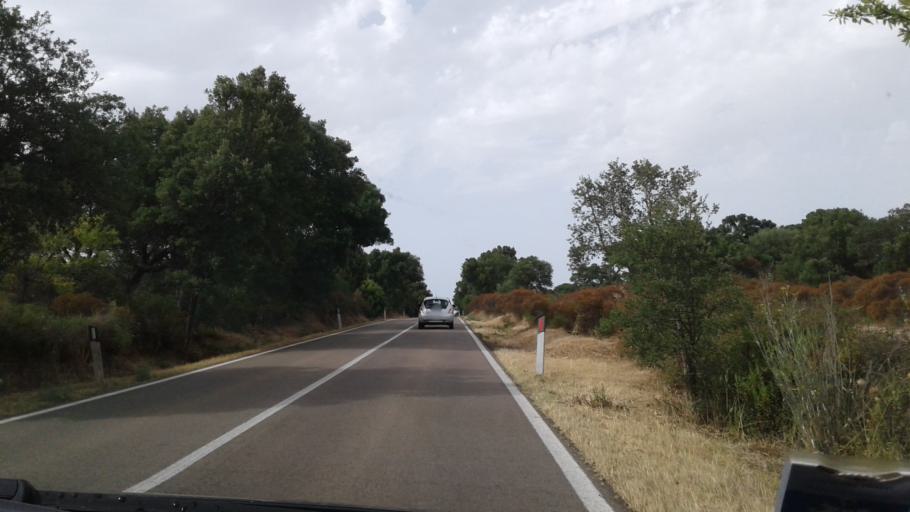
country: IT
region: Sardinia
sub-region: Provincia di Olbia-Tempio
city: Sant'Antonio di Gallura
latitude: 40.9538
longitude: 9.2943
